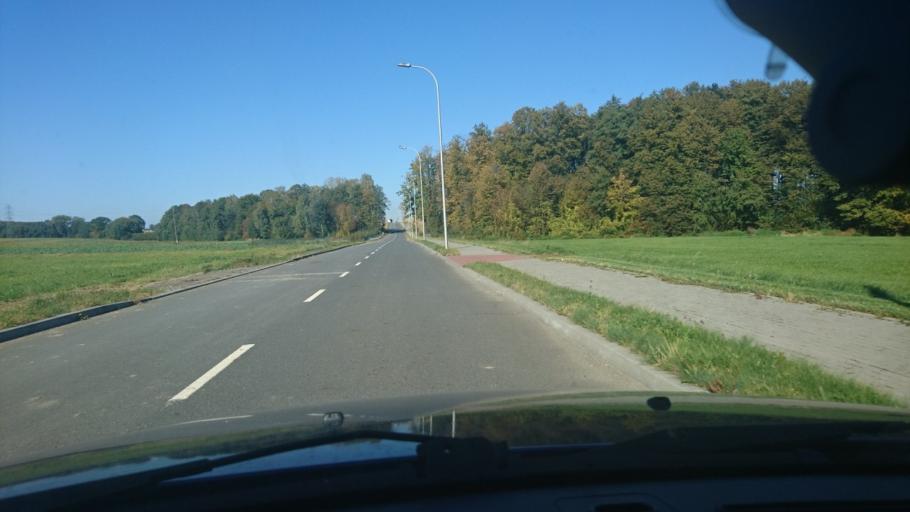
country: PL
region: Silesian Voivodeship
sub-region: Powiat bielski
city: Bronow
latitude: 49.8604
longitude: 18.9432
